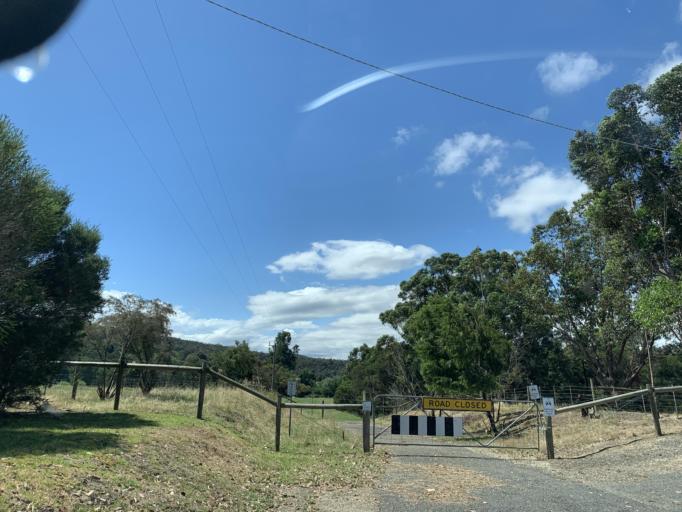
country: AU
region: Victoria
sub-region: Wellington
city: Heyfield
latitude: -37.9997
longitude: 146.6550
